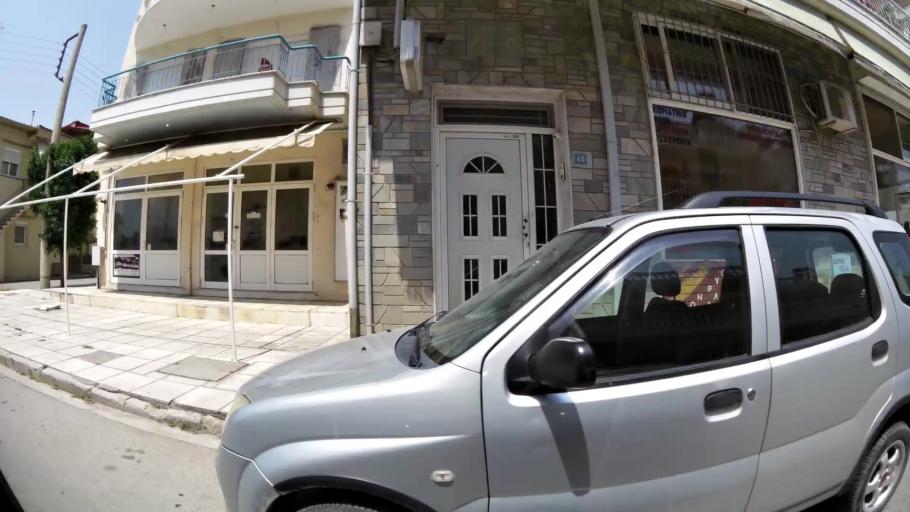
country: GR
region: Central Macedonia
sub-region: Nomos Thessalonikis
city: Evosmos
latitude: 40.6626
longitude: 22.9092
